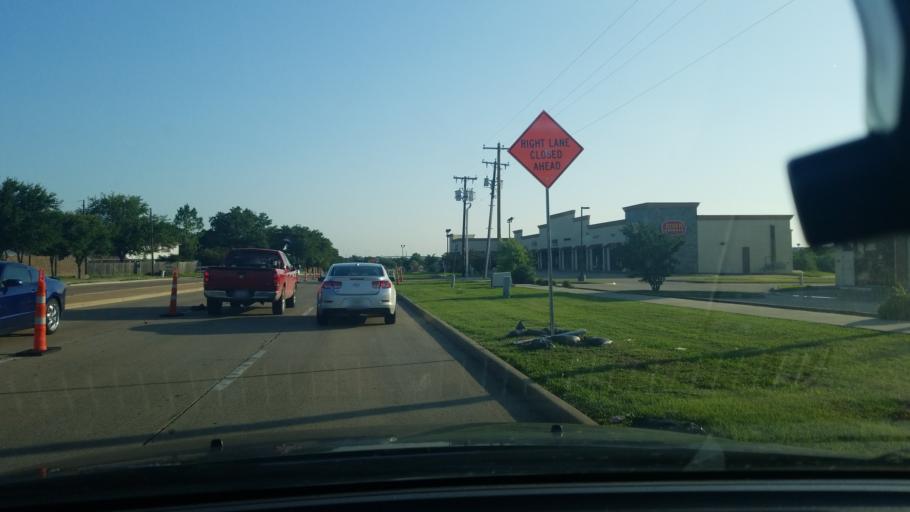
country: US
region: Texas
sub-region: Dallas County
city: Mesquite
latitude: 32.7991
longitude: -96.6339
